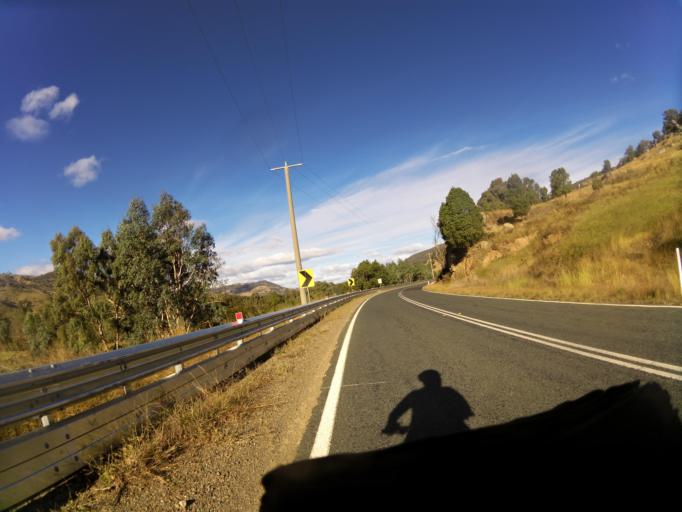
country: AU
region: New South Wales
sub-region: Greater Hume Shire
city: Holbrook
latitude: -35.9651
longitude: 147.7653
